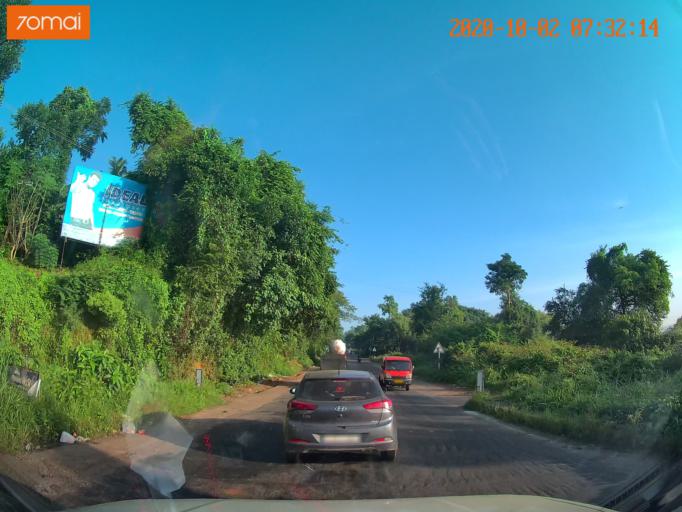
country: IN
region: Kerala
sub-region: Malappuram
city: Pariyapuram
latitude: 11.0526
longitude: 75.9363
